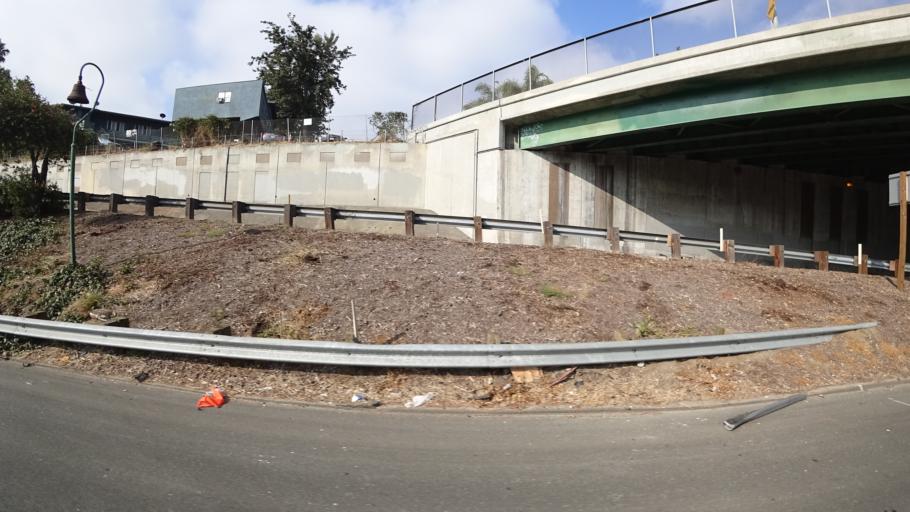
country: US
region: California
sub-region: Los Angeles County
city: Hollywood
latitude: 34.1028
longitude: -118.3178
